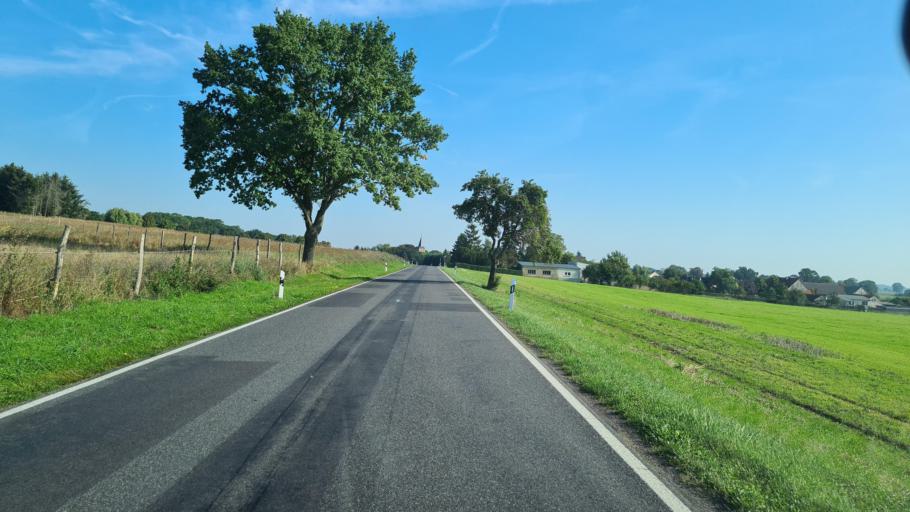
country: DE
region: Brandenburg
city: Pessin
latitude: 52.6857
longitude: 12.6470
